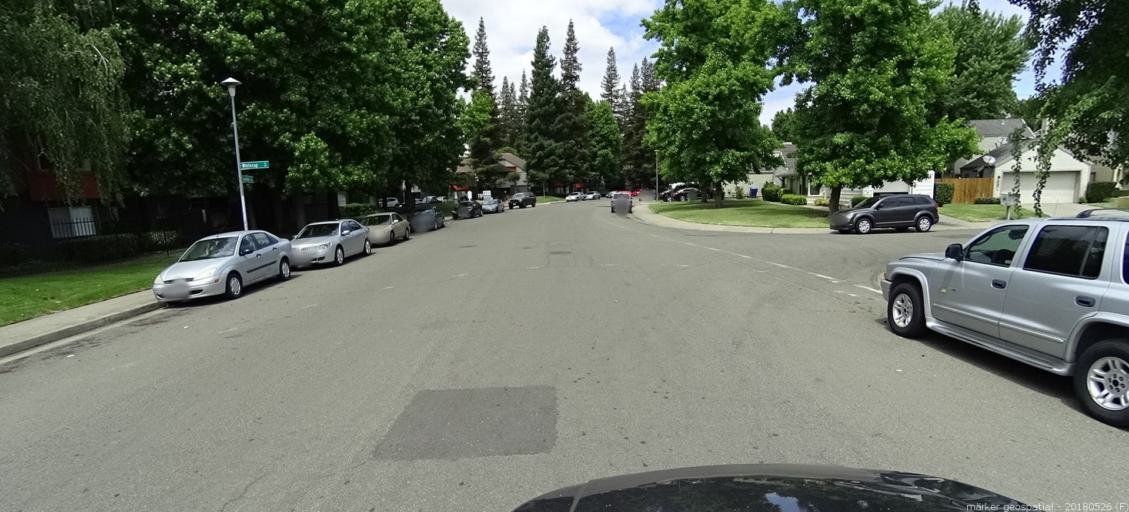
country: US
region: California
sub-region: Sacramento County
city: Sacramento
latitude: 38.6114
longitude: -121.4925
